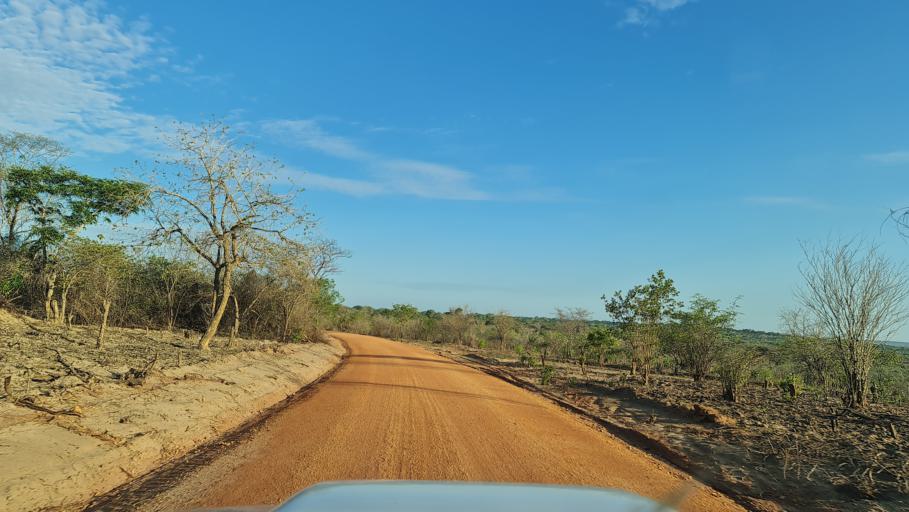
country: MZ
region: Nampula
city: Nacala
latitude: -14.6946
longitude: 40.3201
